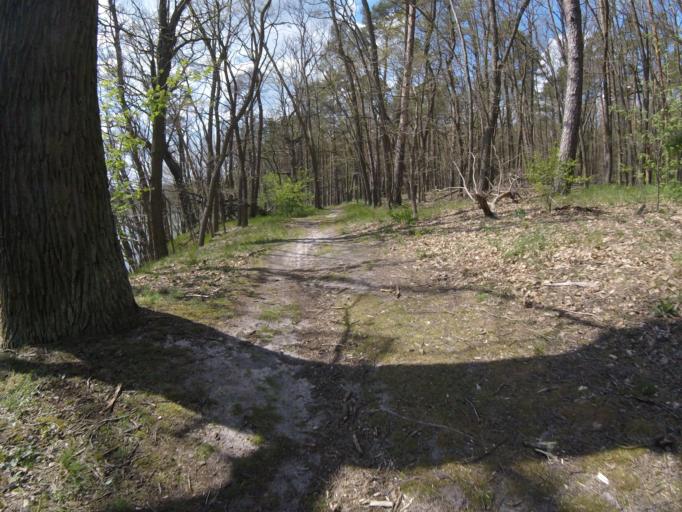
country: DE
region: Brandenburg
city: Gross Koris
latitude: 52.2004
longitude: 13.7181
